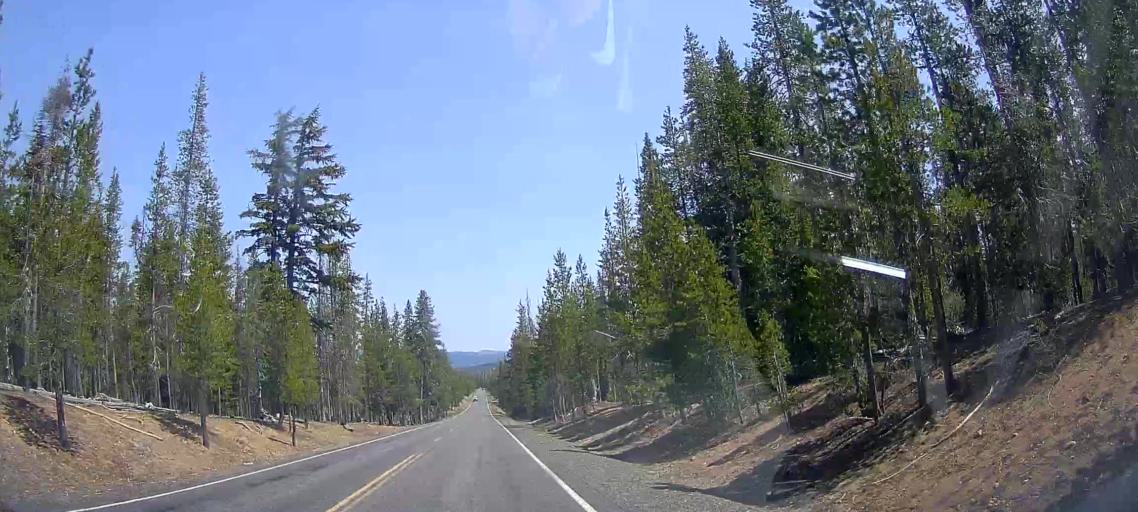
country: US
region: Oregon
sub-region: Jackson County
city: Shady Cove
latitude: 43.0166
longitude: -122.1262
